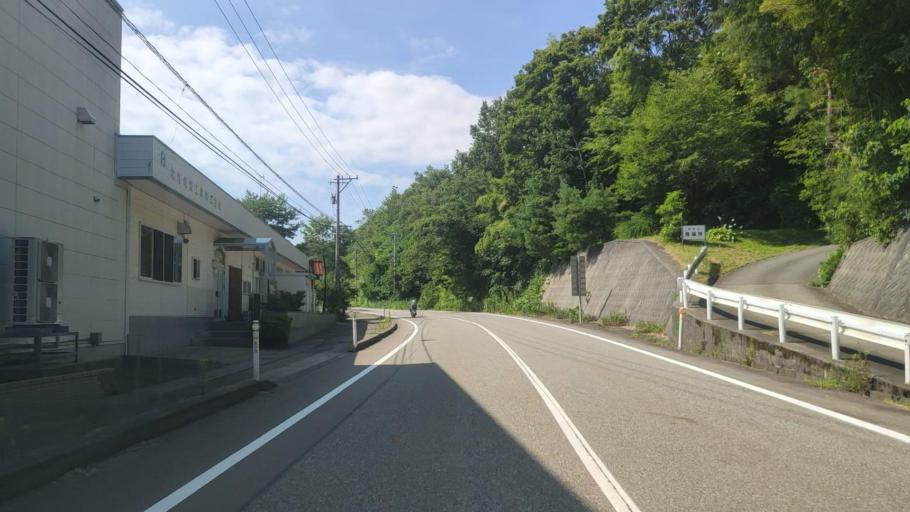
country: JP
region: Ishikawa
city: Komatsu
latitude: 36.3871
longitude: 136.4957
